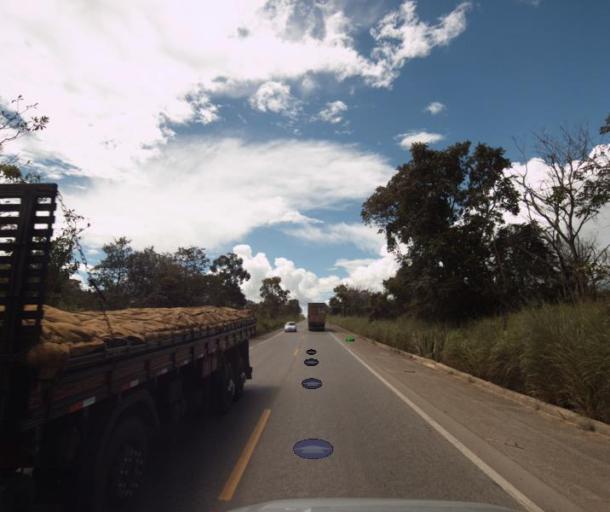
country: BR
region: Goias
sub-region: Uruacu
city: Uruacu
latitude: -14.1333
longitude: -49.1123
